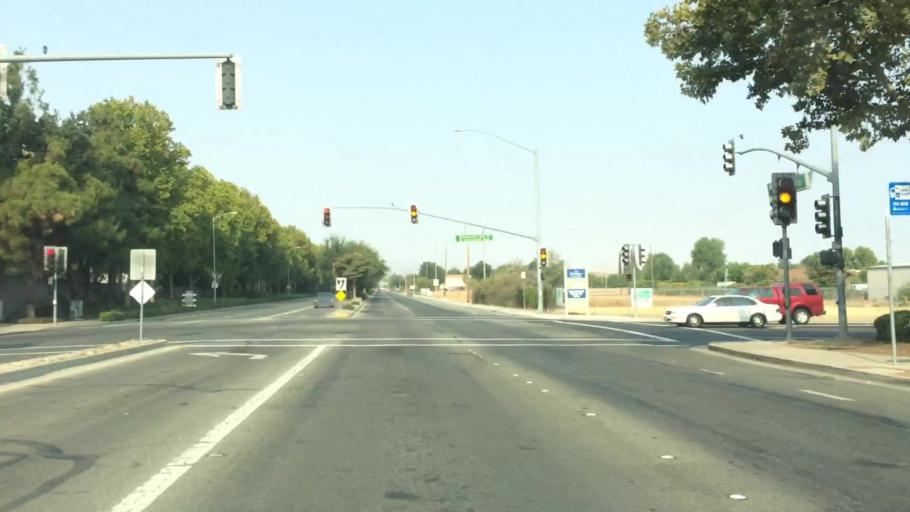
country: US
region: California
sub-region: Contra Costa County
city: Brentwood
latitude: 37.9254
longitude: -121.7142
